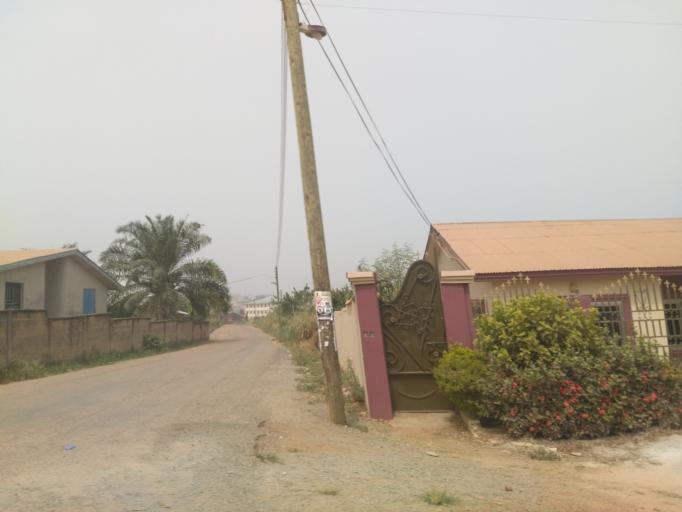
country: GH
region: Ashanti
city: Mamponteng
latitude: 6.6658
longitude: -1.5440
